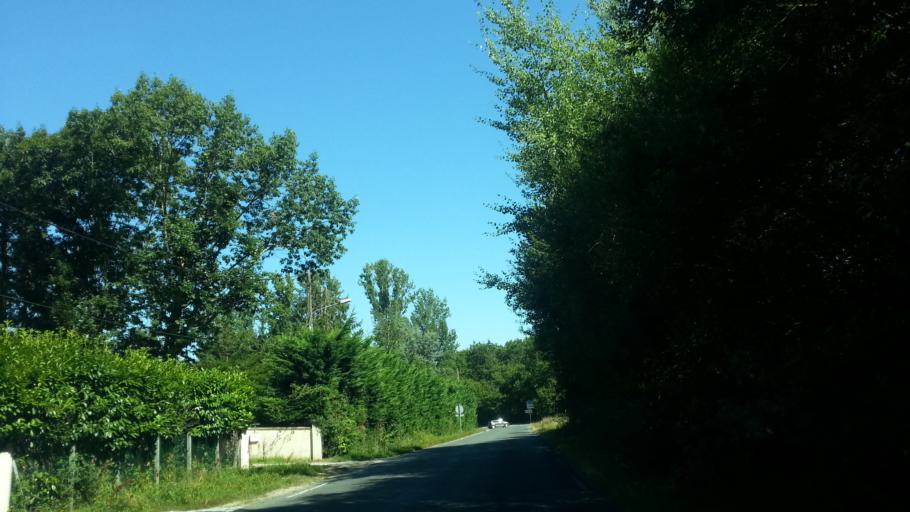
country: FR
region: Aquitaine
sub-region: Departement de la Gironde
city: Saint-Selve
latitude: 44.6875
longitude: -0.5087
